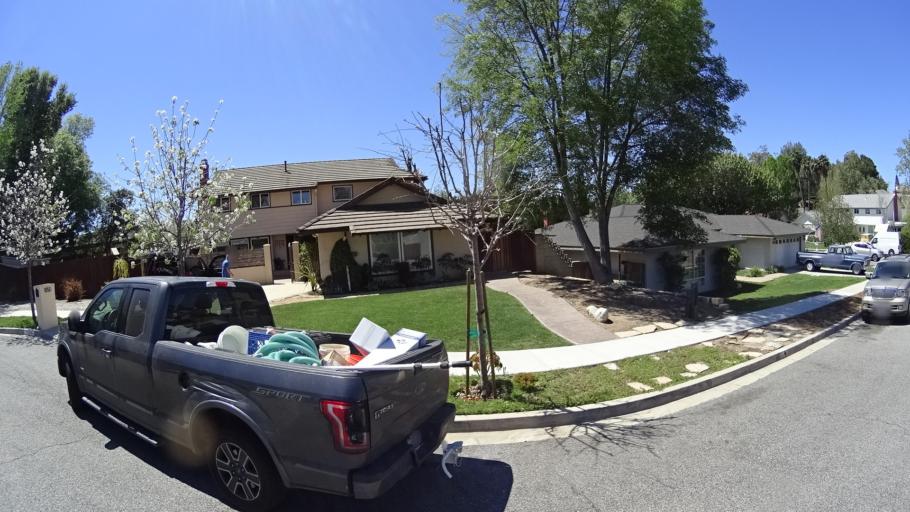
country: US
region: California
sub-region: Ventura County
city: Thousand Oaks
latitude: 34.1962
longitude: -118.8432
